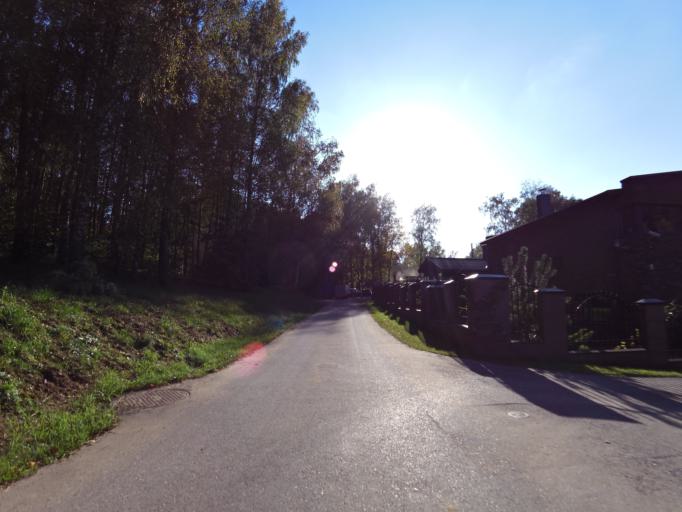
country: LT
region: Vilnius County
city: Pilaite
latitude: 54.7199
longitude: 25.1925
